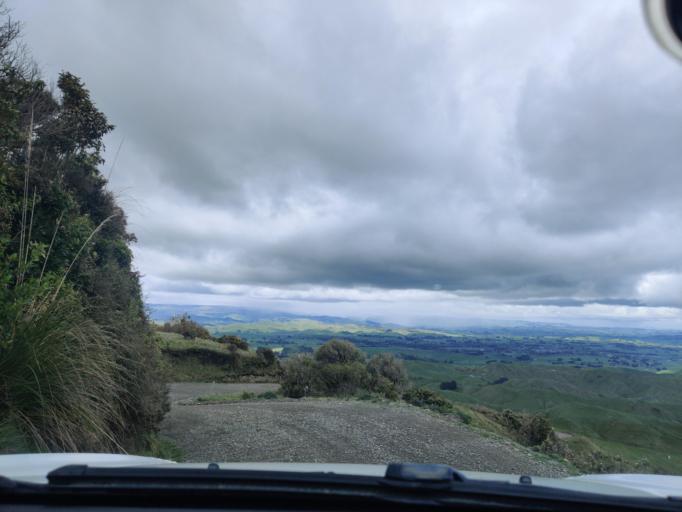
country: NZ
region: Manawatu-Wanganui
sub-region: Palmerston North City
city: Palmerston North
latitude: -40.2750
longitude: 175.8517
